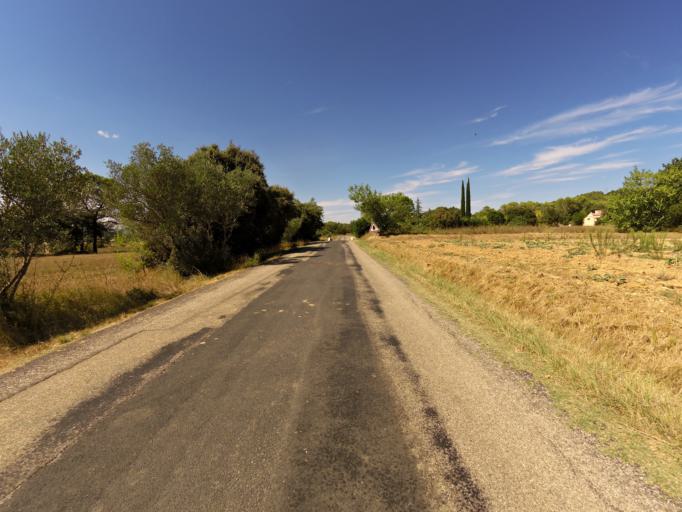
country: FR
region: Languedoc-Roussillon
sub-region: Departement du Gard
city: Quissac
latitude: 43.8926
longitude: 4.0485
